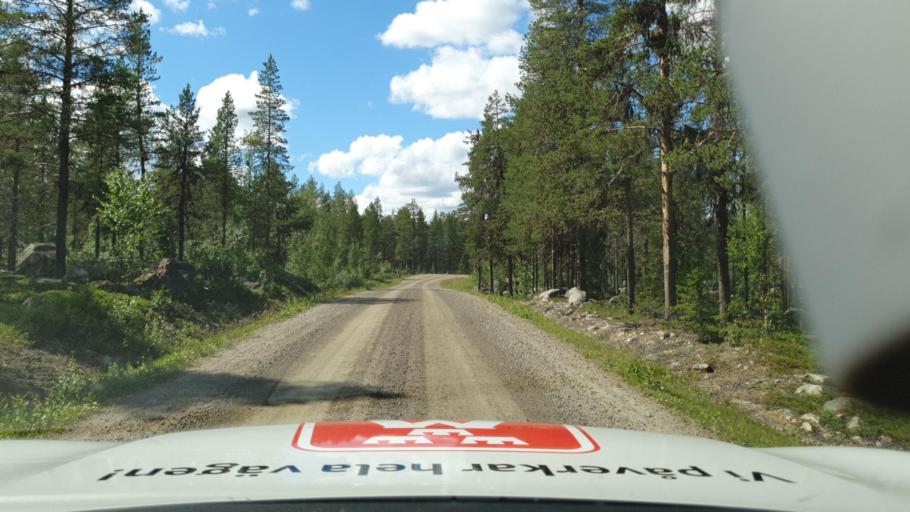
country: SE
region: Vaesterbotten
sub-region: Sorsele Kommun
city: Sorsele
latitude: 65.6711
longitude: 17.2651
